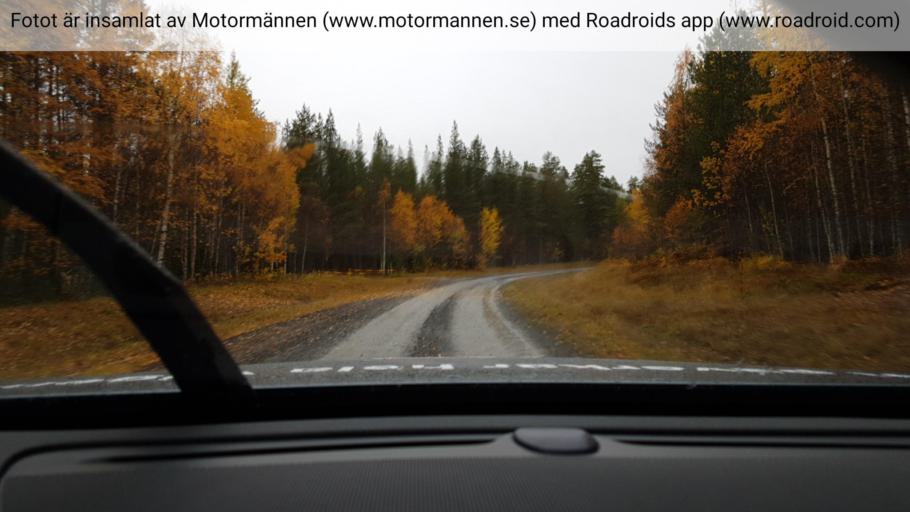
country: SE
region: Norrbotten
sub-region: Pajala Kommun
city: Pajala
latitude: 66.9823
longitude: 22.8765
